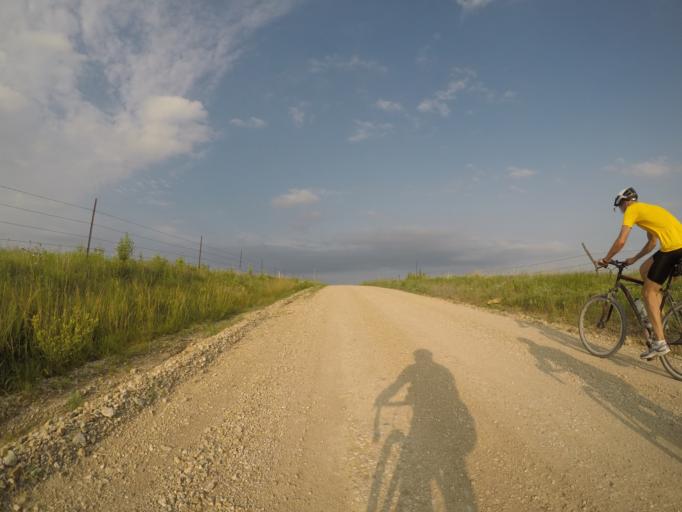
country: US
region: Kansas
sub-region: Wabaunsee County
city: Alma
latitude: 39.1016
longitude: -96.3681
